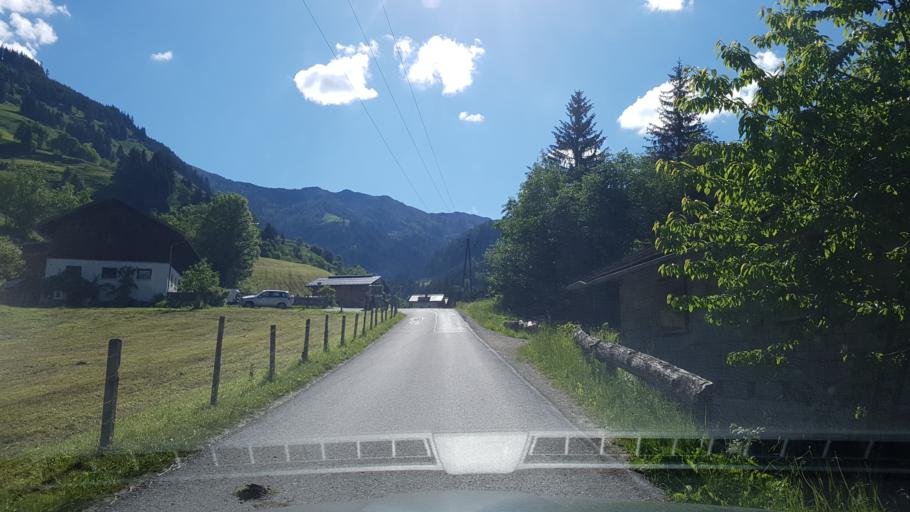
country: AT
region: Salzburg
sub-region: Politischer Bezirk Sankt Johann im Pongau
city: Huttschlag
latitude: 47.2353
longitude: 13.2412
